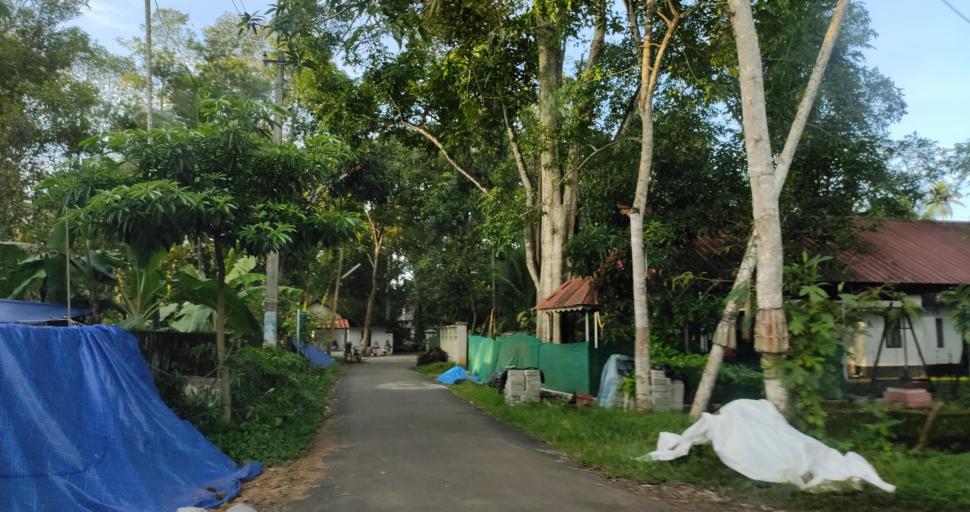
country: IN
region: Kerala
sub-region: Alappuzha
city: Shertallai
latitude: 9.6034
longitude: 76.3630
